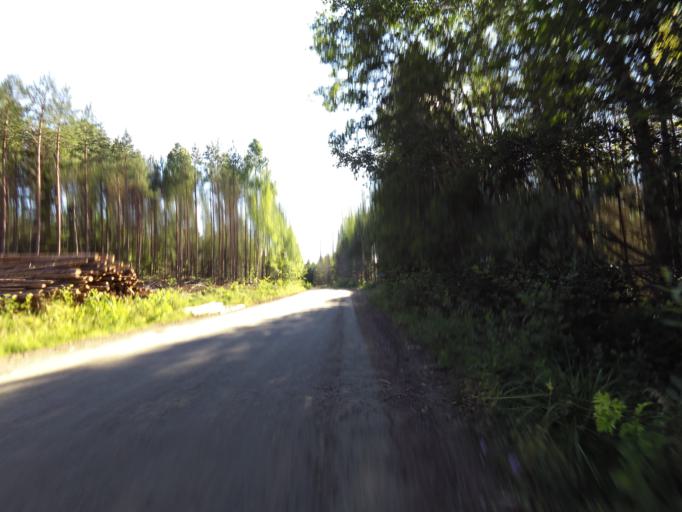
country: SE
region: Gaevleborg
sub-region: Hofors Kommun
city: Hofors
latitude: 60.5914
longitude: 16.2614
